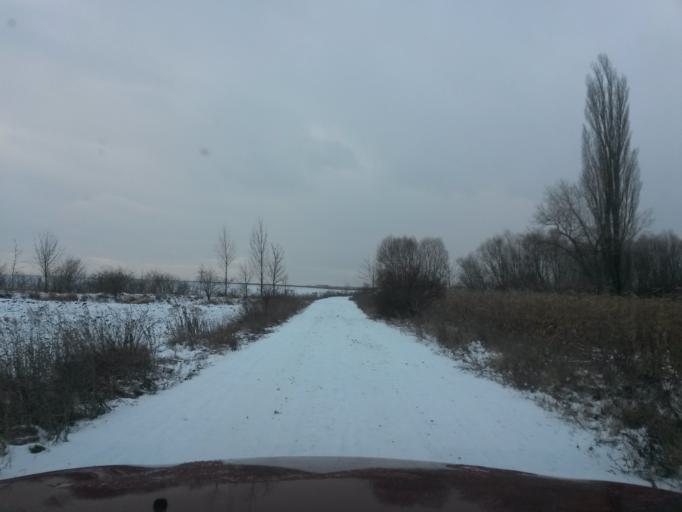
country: SK
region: Kosicky
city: Kosice
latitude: 48.6345
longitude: 21.2922
